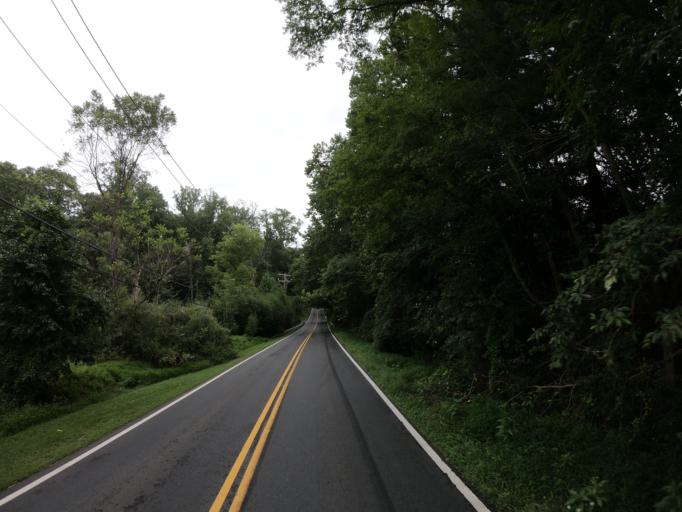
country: US
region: Maryland
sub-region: Montgomery County
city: Montgomery Village
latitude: 39.2009
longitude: -77.2015
